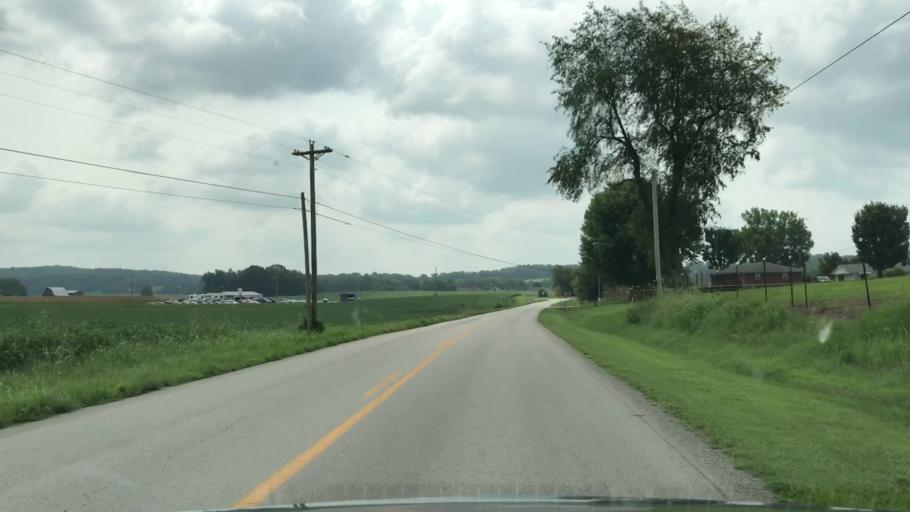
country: US
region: Kentucky
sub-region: Barren County
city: Cave City
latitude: 37.0991
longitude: -85.9755
